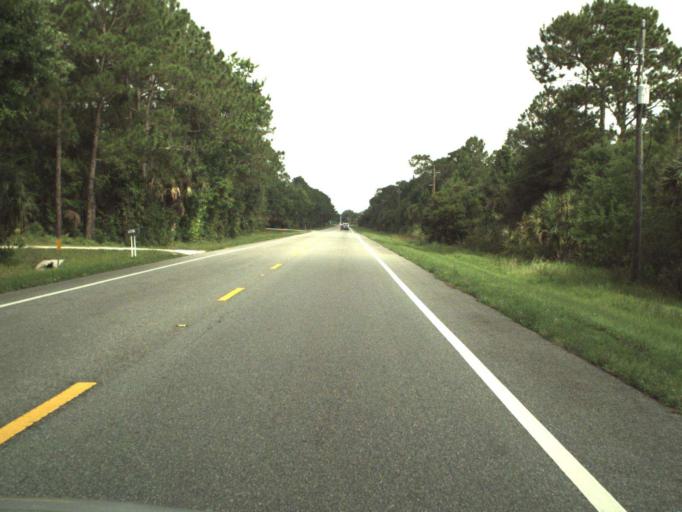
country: US
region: Florida
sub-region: Seminole County
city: Geneva
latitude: 28.7738
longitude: -81.1601
